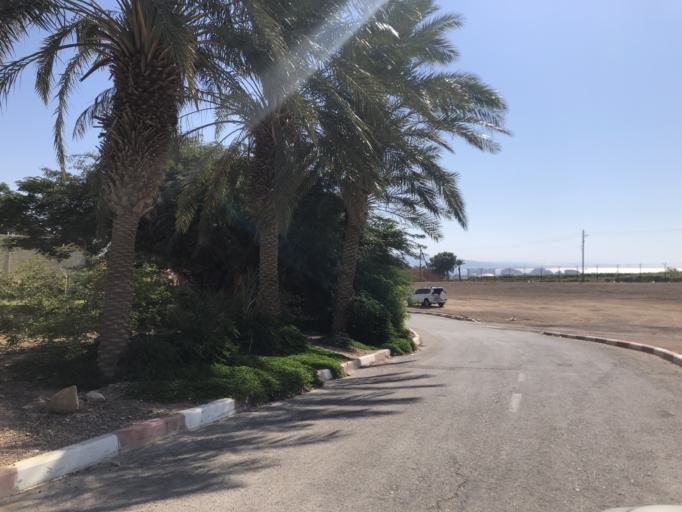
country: IL
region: Southern District
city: Eilat
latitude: 29.5815
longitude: 34.9605
